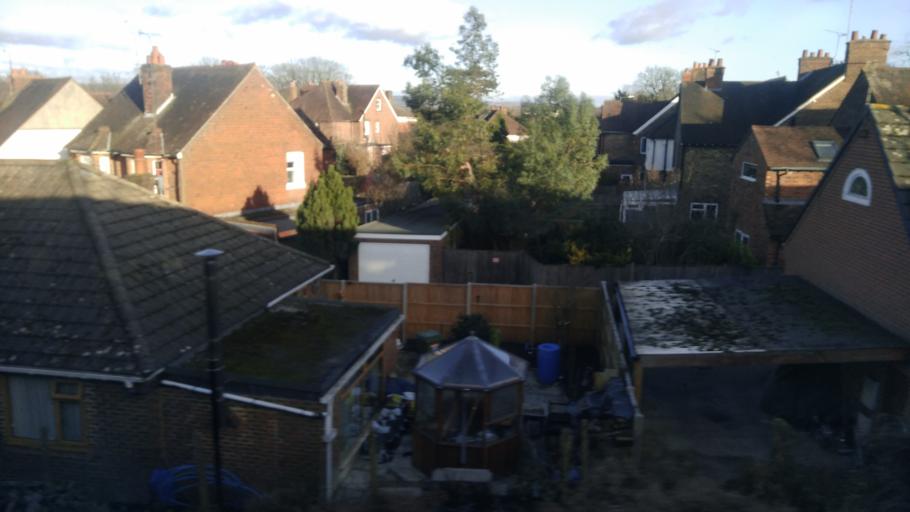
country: GB
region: England
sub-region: Kent
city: Sevenoaks
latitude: 51.2856
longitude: 0.1714
